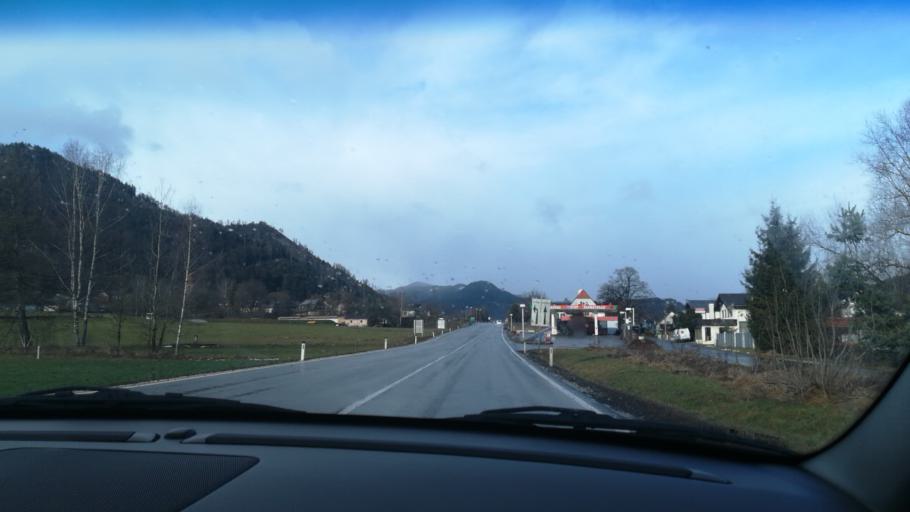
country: AT
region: Styria
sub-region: Politischer Bezirk Murtal
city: Sankt Peter ob Judenburg
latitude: 47.1835
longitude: 14.5971
